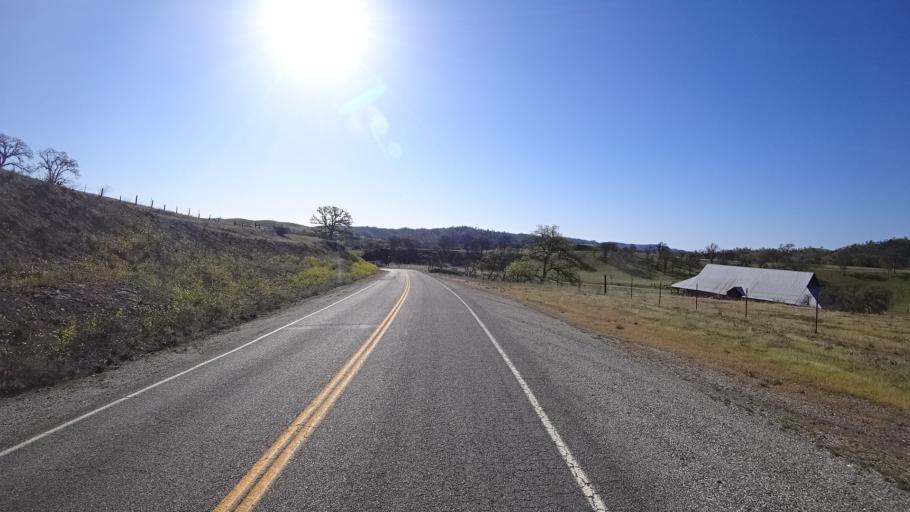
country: US
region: California
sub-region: Glenn County
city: Orland
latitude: 39.6837
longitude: -122.5383
